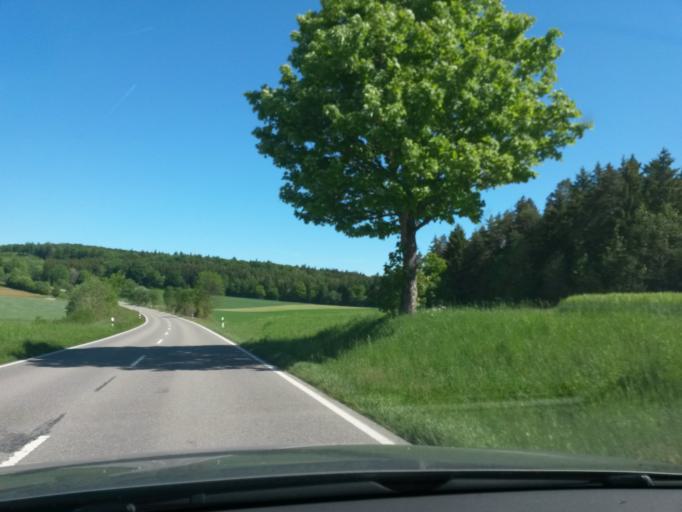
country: DE
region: Baden-Wuerttemberg
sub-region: Tuebingen Region
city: Trochtelfingen
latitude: 48.2785
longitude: 9.2765
